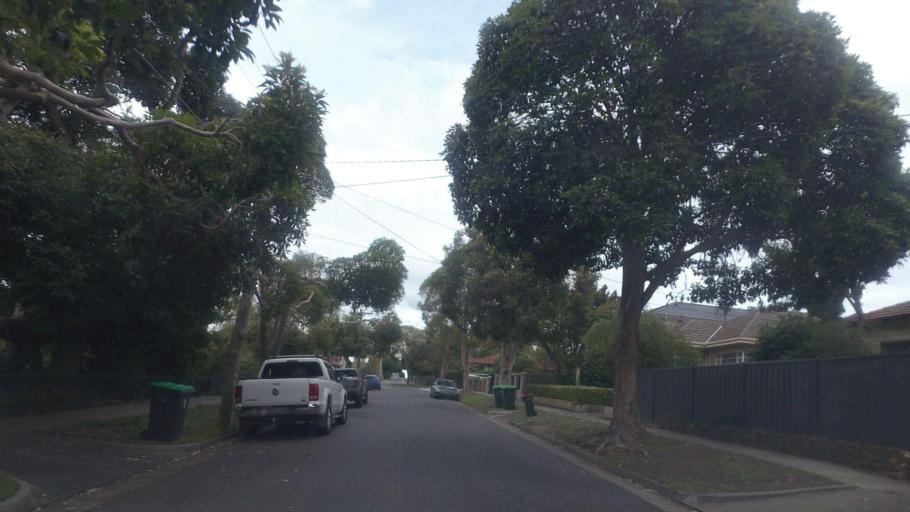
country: AU
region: Victoria
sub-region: Whitehorse
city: Box Hill South
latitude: -37.8299
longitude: 145.1159
